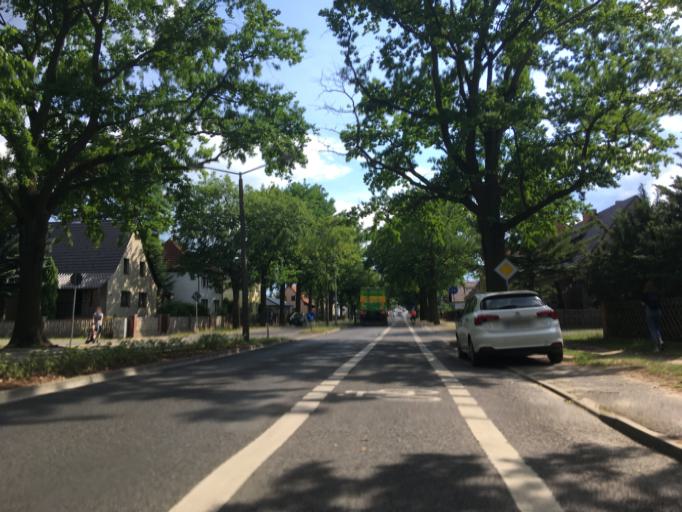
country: DE
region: Brandenburg
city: Furstenwalde
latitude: 52.3691
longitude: 14.0714
